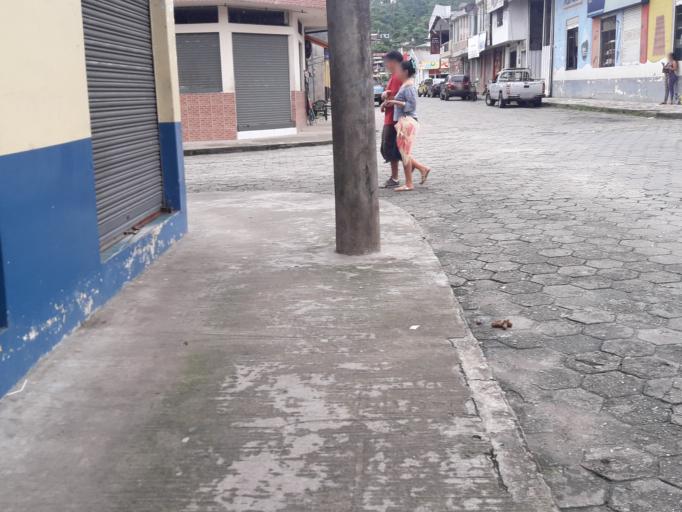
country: EC
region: Napo
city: Tena
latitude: -1.0007
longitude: -77.8124
